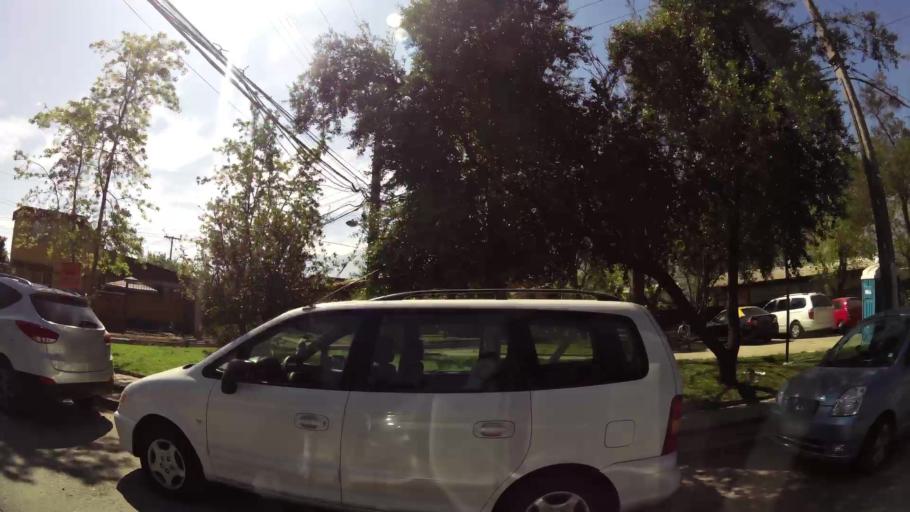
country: CL
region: Santiago Metropolitan
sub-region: Provincia de Santiago
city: Villa Presidente Frei, Nunoa, Santiago, Chile
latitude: -33.4488
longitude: -70.5404
